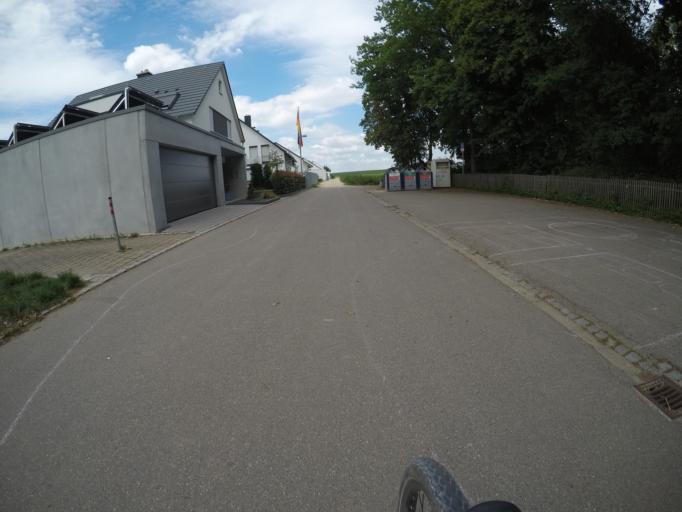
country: DE
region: Baden-Wuerttemberg
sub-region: Regierungsbezirk Stuttgart
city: Kongen
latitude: 48.6915
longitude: 9.3674
